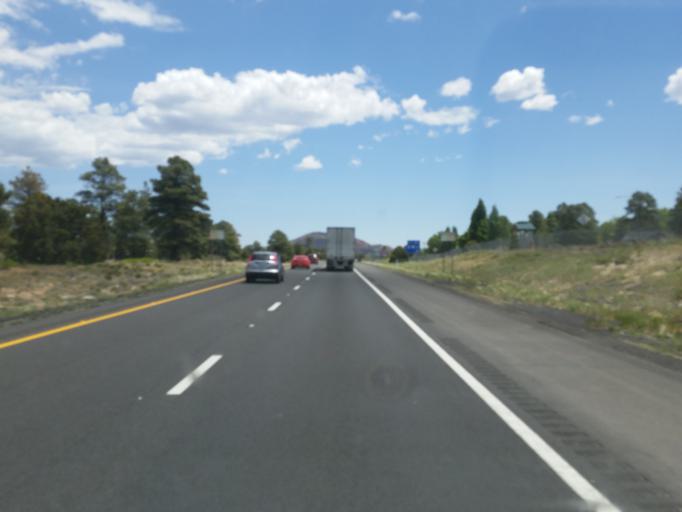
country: US
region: Arizona
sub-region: Coconino County
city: Flagstaff
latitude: 35.2072
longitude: -111.6007
